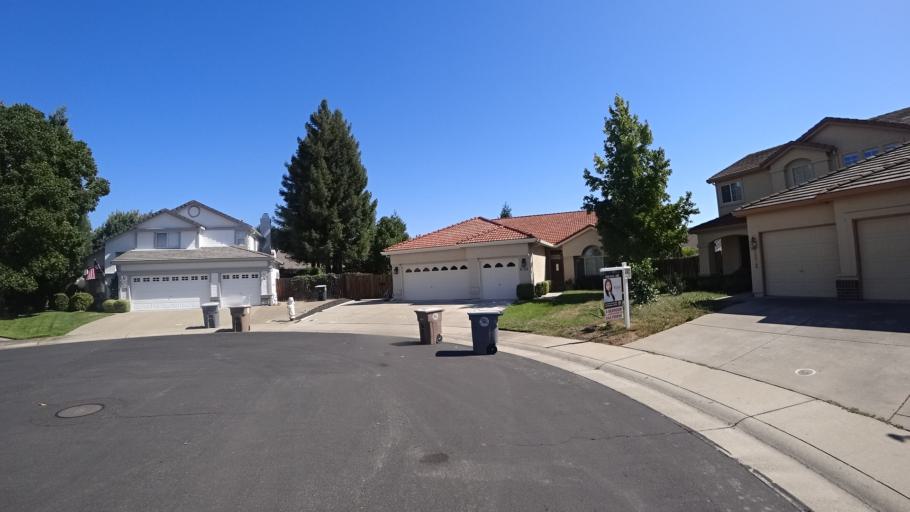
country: US
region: California
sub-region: Sacramento County
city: Laguna
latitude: 38.4375
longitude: -121.4291
